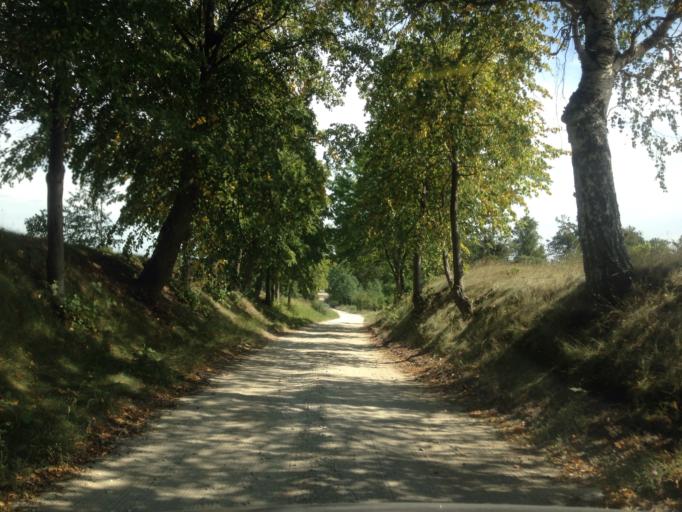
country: PL
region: Kujawsko-Pomorskie
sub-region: Powiat brodnicki
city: Gorzno
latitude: 53.2005
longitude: 19.6355
